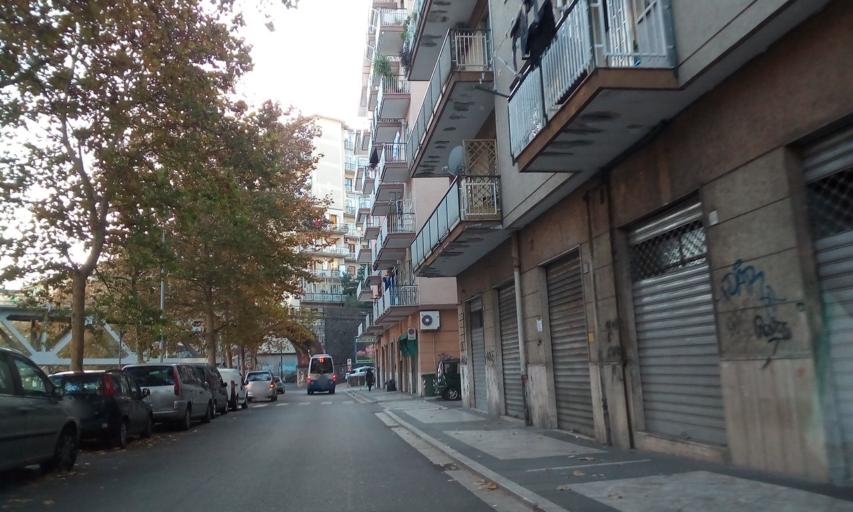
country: IT
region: Campania
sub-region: Provincia di Salerno
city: Capezzano Inferiore
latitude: 40.6832
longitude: 14.7744
